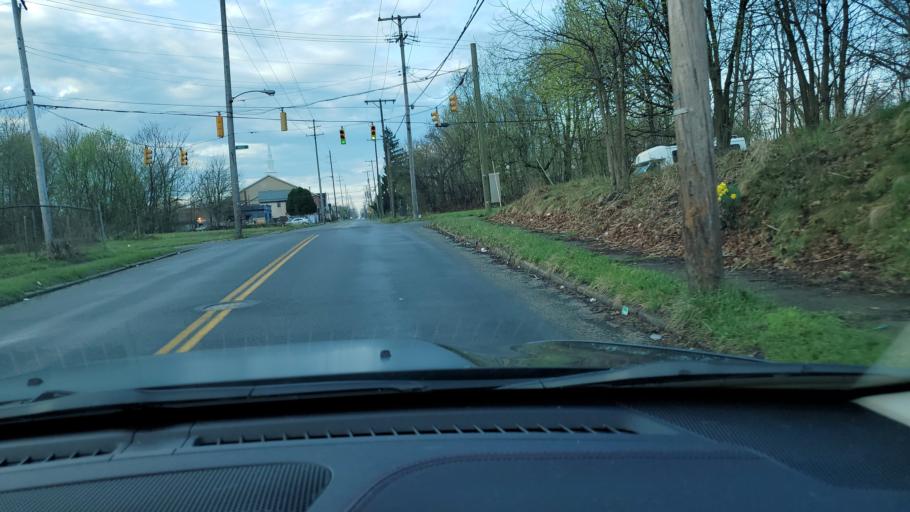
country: US
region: Ohio
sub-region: Mahoning County
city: Youngstown
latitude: 41.0880
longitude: -80.6640
